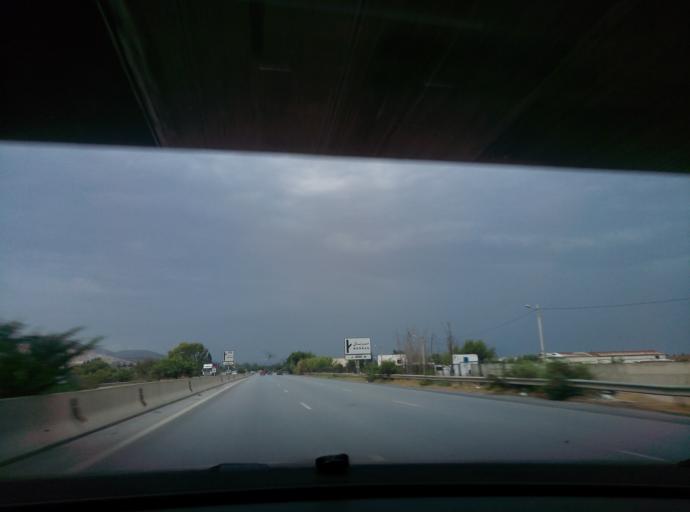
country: TN
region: Tunis
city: La Sebala du Mornag
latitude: 36.7088
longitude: 10.2872
